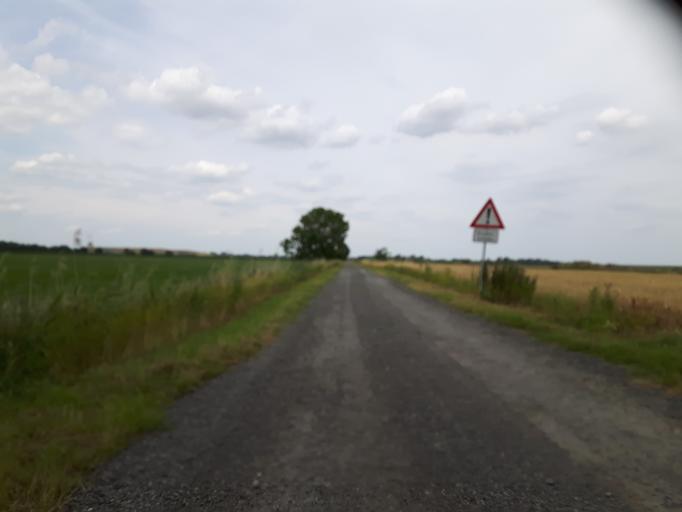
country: DE
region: Lower Saxony
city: Varel
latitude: 53.3891
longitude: 8.2002
